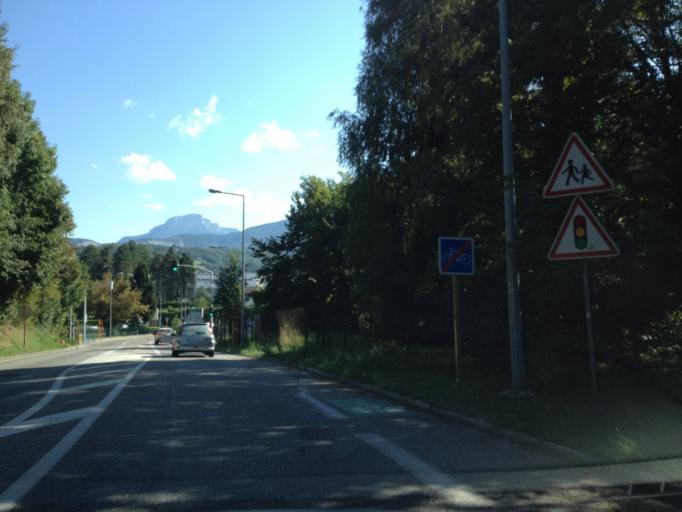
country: FR
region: Rhone-Alpes
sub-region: Departement de la Savoie
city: Cognin
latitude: 45.5653
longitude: 5.9032
